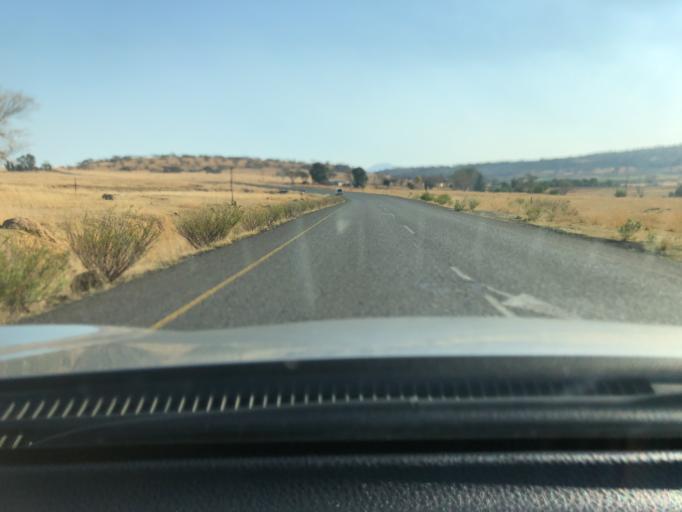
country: ZA
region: KwaZulu-Natal
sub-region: uThukela District Municipality
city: Ekuvukeni
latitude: -28.3381
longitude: 30.0407
